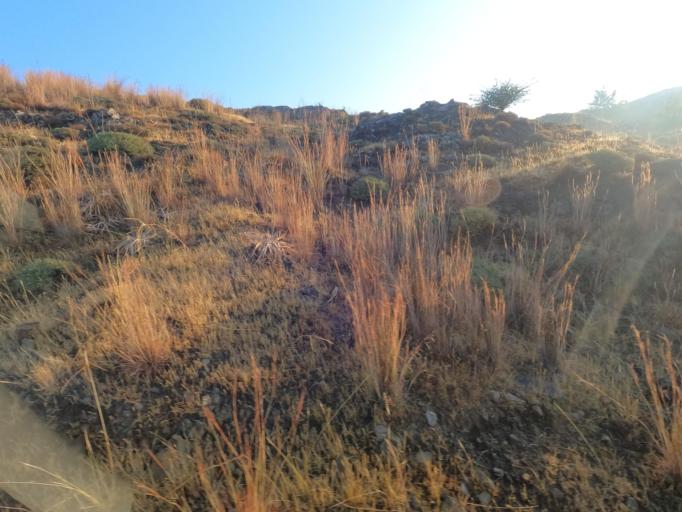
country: CY
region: Larnaka
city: Mosfiloti
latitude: 34.9745
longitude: 33.4217
